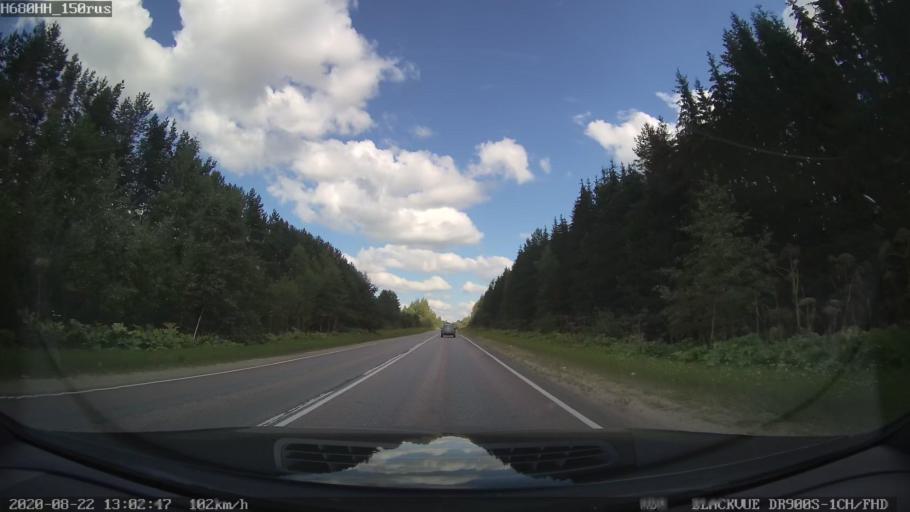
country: RU
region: Tverskaya
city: Bezhetsk
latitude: 57.6532
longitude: 36.4018
